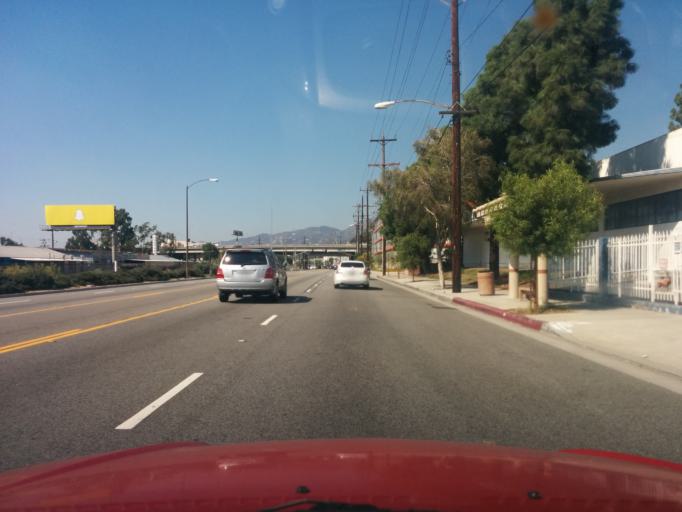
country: US
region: California
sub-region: Los Angeles County
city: North Glendale
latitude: 34.1514
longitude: -118.2741
